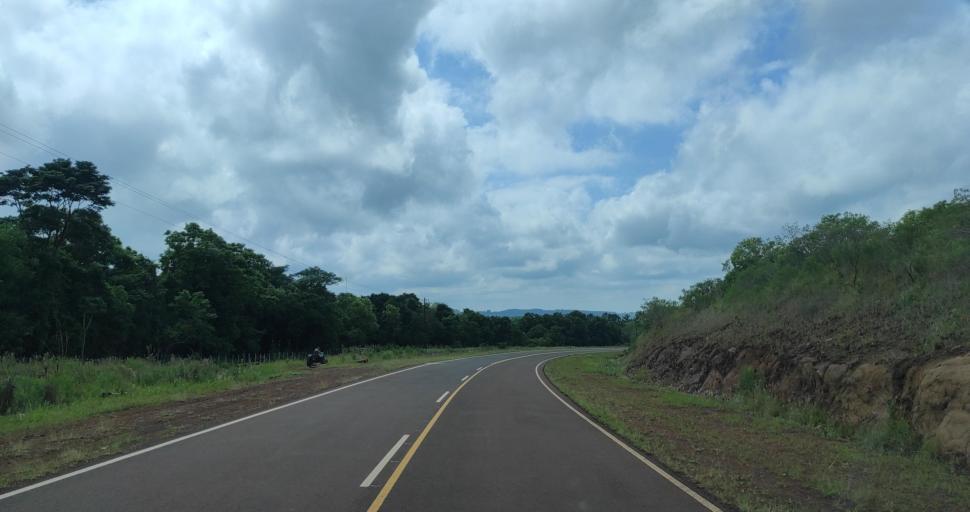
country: AR
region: Misiones
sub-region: Departamento de Veinticinco de Mayo
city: Veinticinco de Mayo
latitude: -27.3752
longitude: -54.8571
